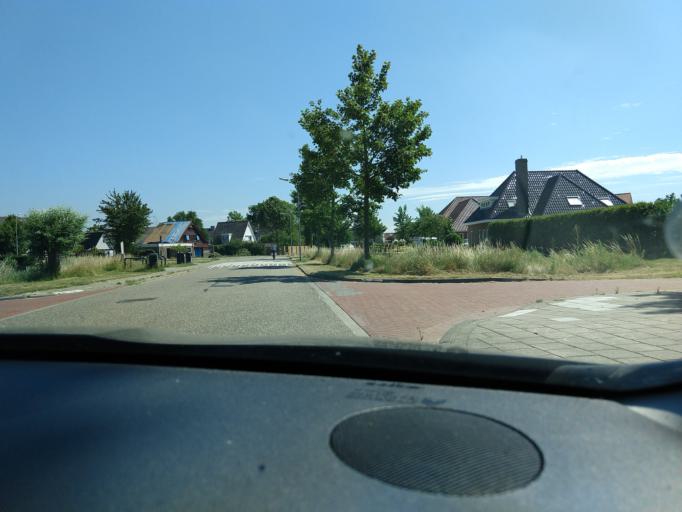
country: NL
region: Zeeland
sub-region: Gemeente Veere
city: Veere
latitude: 51.5062
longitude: 3.6706
